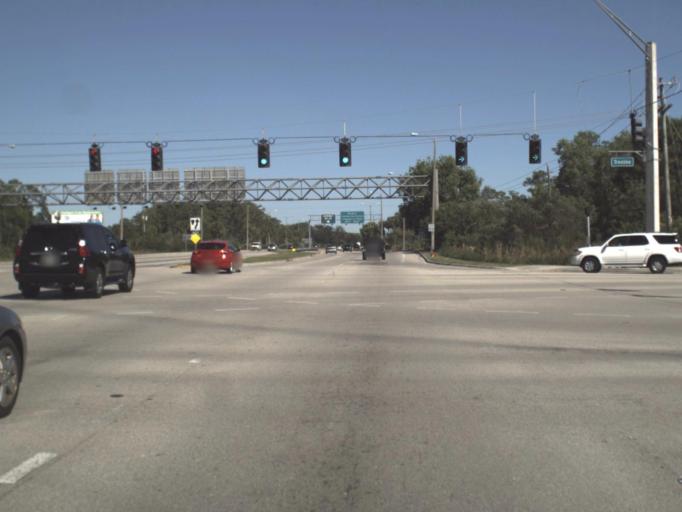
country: US
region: Florida
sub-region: Lee County
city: Gateway
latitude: 26.5473
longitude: -81.7866
